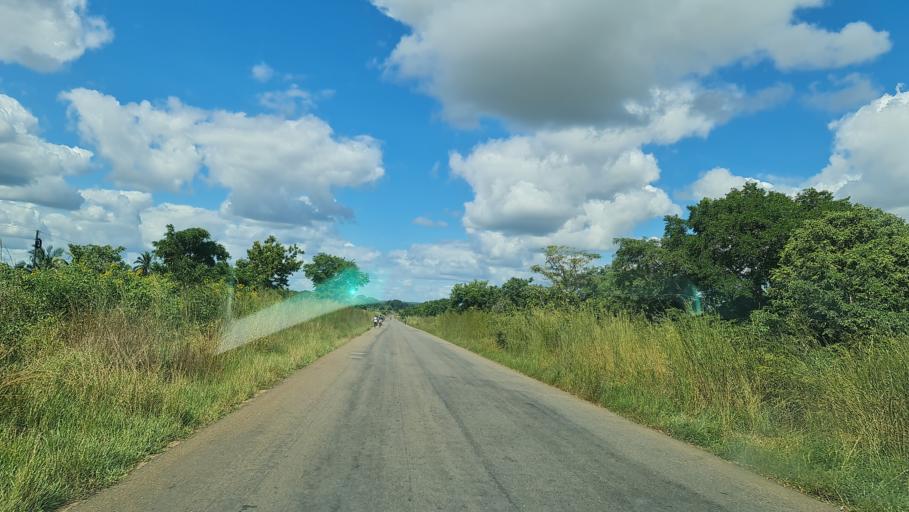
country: MZ
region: Zambezia
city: Quelimane
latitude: -17.5100
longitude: 36.2531
